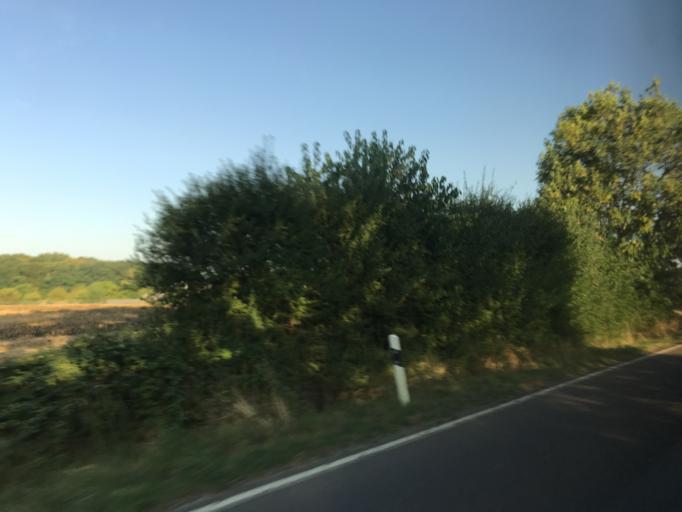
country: LU
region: Luxembourg
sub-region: Canton d'Esch-sur-Alzette
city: Frisange
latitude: 49.5245
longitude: 6.1843
